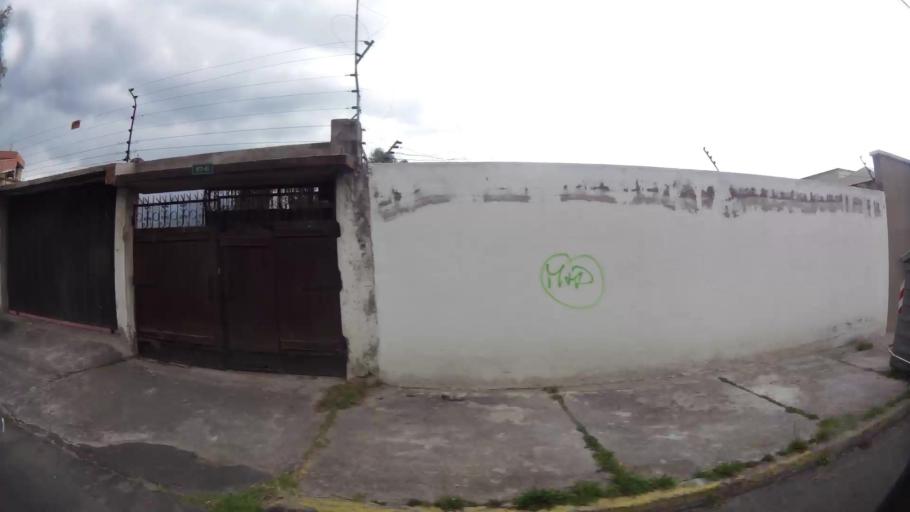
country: EC
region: Pichincha
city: Quito
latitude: -0.1006
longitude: -78.4822
